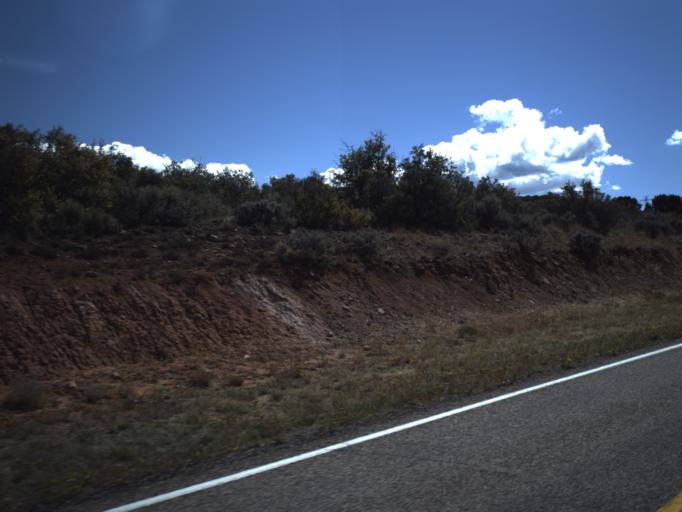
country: US
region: Utah
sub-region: Washington County
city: Enterprise
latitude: 37.4836
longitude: -113.6290
